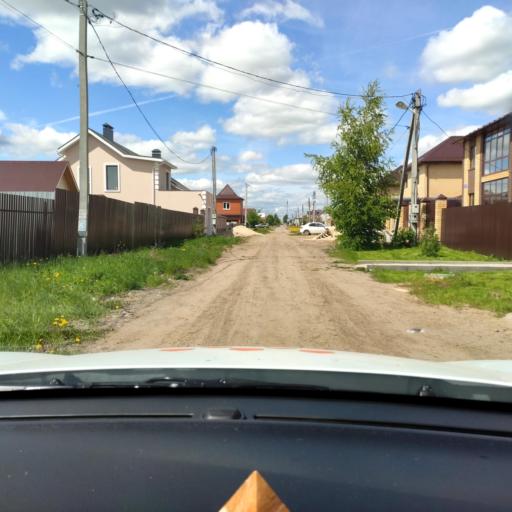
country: RU
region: Tatarstan
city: Osinovo
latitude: 55.8781
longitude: 48.8706
